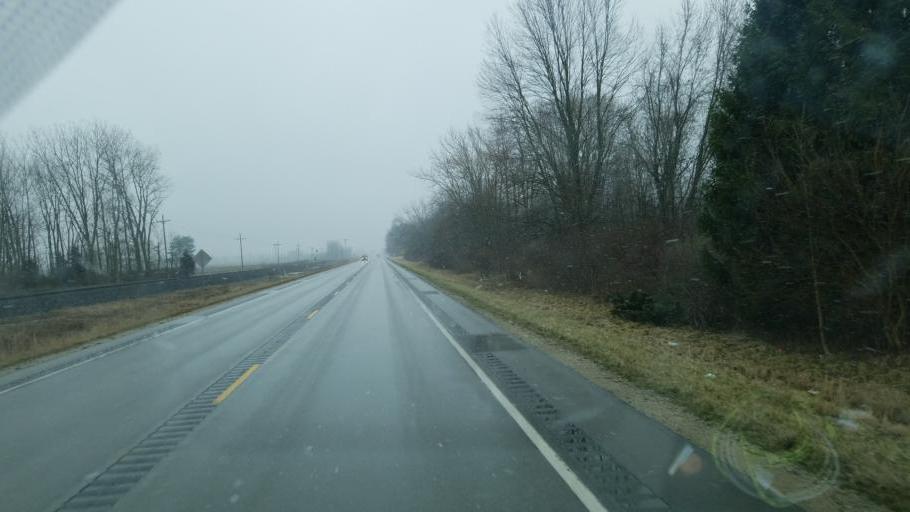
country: US
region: Indiana
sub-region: Wabash County
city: Mount Vernon
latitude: 40.6984
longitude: -85.7523
